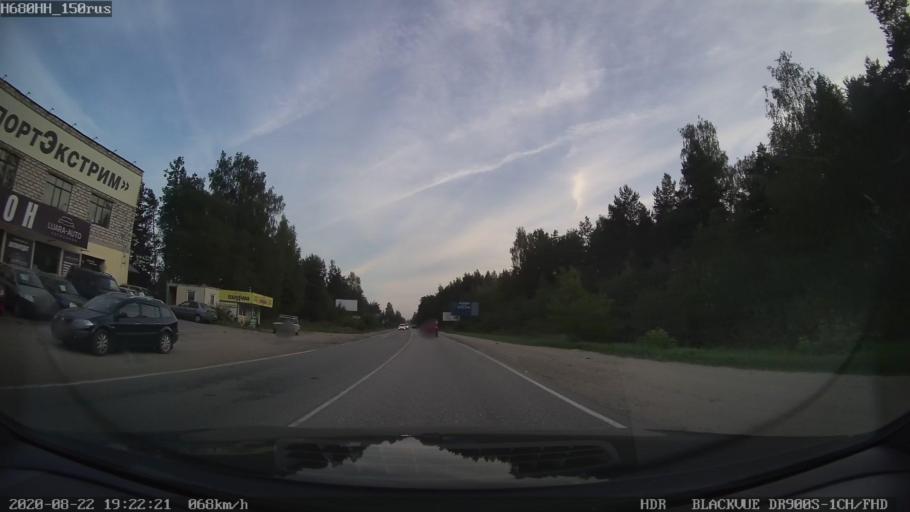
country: RU
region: Tverskaya
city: Tver
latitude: 56.9045
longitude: 35.9350
